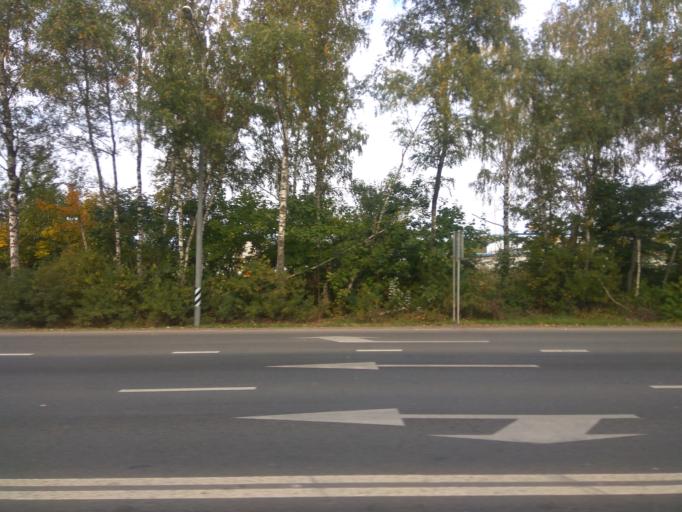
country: RU
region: Moskovskaya
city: Medvezh'i Ozera
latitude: 55.8506
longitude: 37.9683
